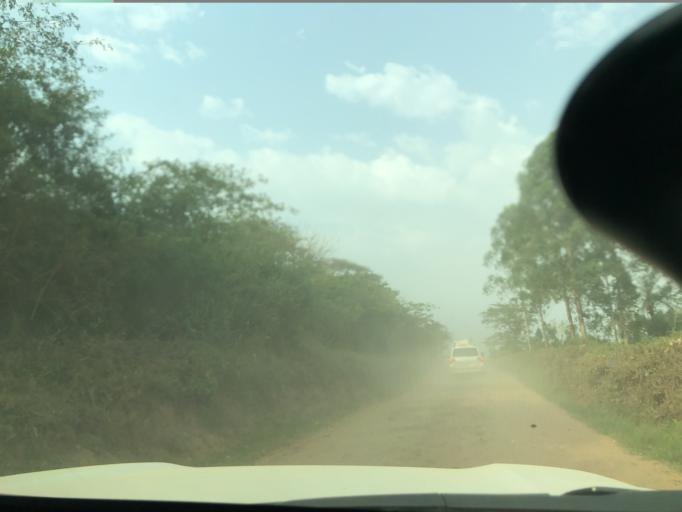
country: UG
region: Western Region
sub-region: Kasese District
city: Margherita
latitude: 0.2037
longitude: 29.6728
